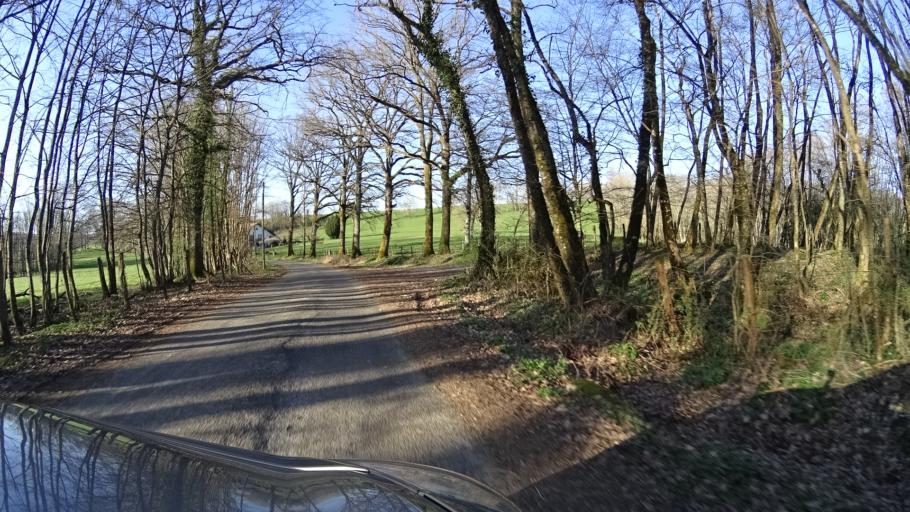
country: FR
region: Franche-Comte
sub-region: Departement du Doubs
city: Morre
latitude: 47.1890
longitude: 6.0552
